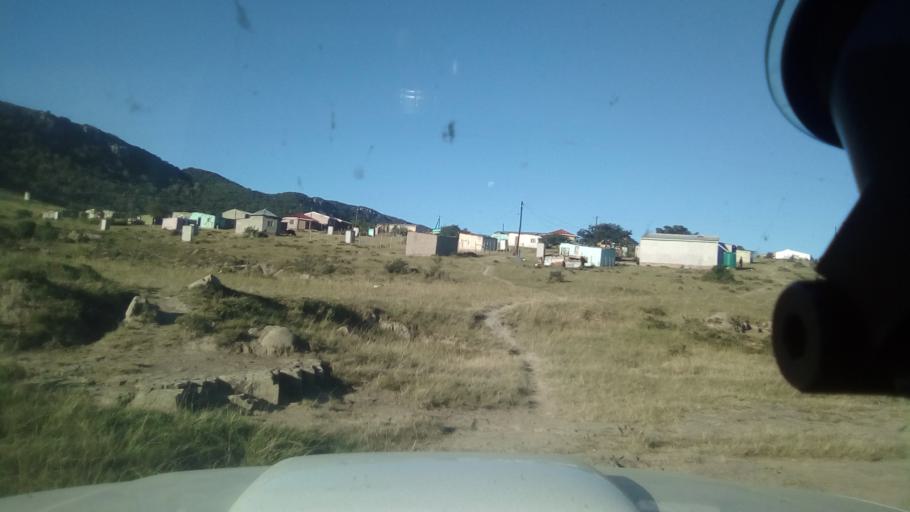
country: ZA
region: Eastern Cape
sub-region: Buffalo City Metropolitan Municipality
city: Bhisho
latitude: -32.7324
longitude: 27.3653
